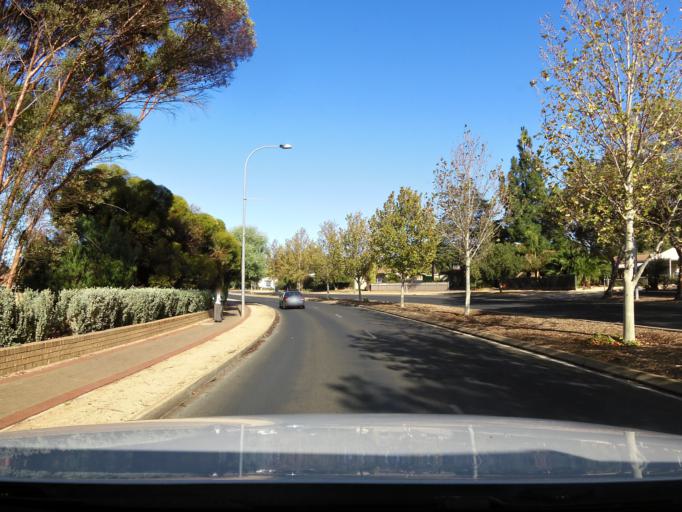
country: AU
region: South Australia
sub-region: Berri and Barmera
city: Berri
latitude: -34.2812
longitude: 140.6068
